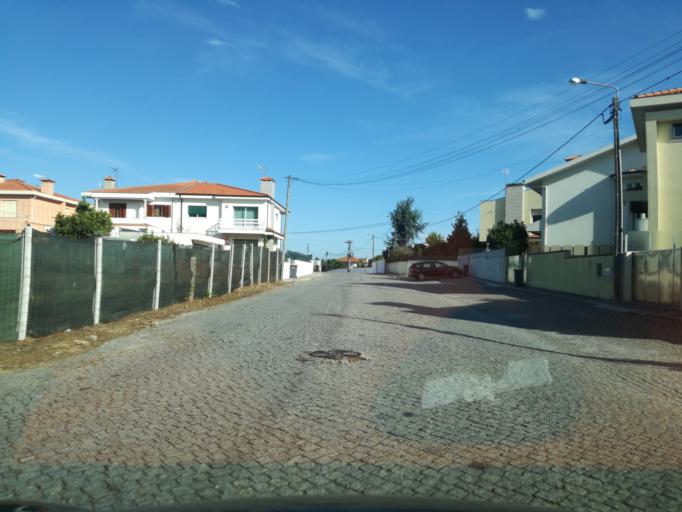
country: PT
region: Porto
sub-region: Maia
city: Nogueira
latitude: 41.2618
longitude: -8.5972
